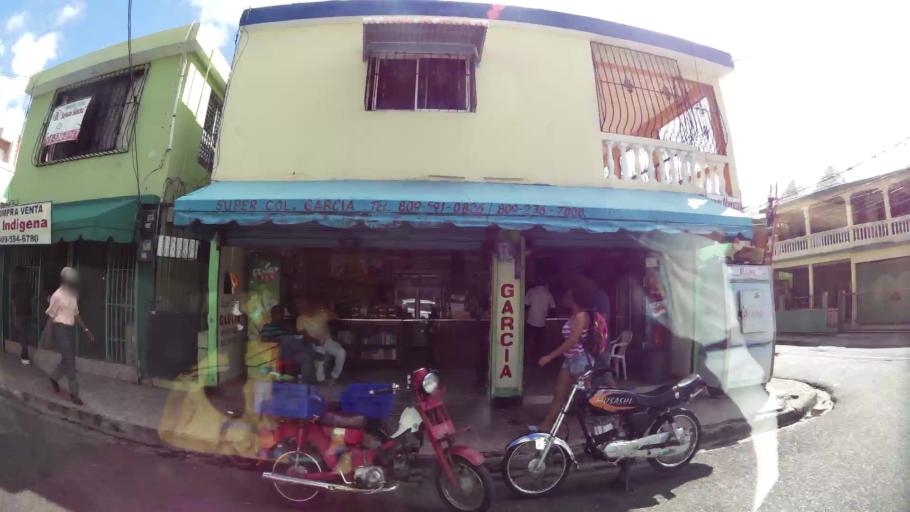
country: DO
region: Santo Domingo
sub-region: Santo Domingo
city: Santo Domingo Este
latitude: 18.5097
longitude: -69.8497
